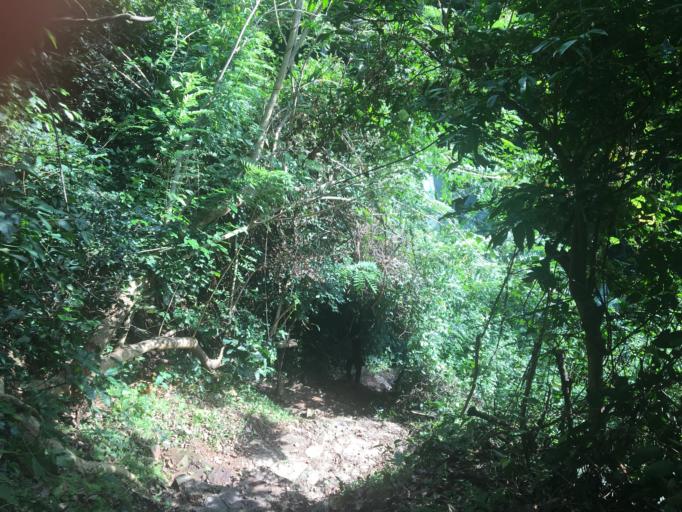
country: TG
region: Plateaux
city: Kpalime
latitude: 6.8577
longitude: 0.5544
